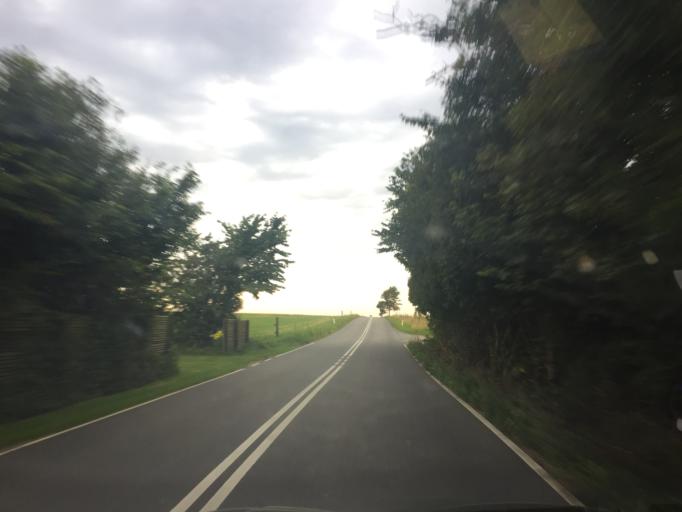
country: DK
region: Capital Region
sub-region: Egedal Kommune
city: Stenlose
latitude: 55.7314
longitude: 12.1991
